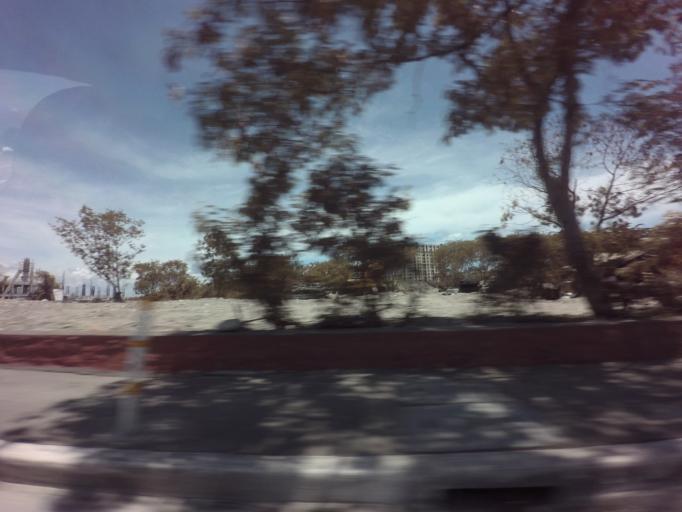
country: PH
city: Sambayanihan People's Village
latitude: 14.4906
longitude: 120.9984
